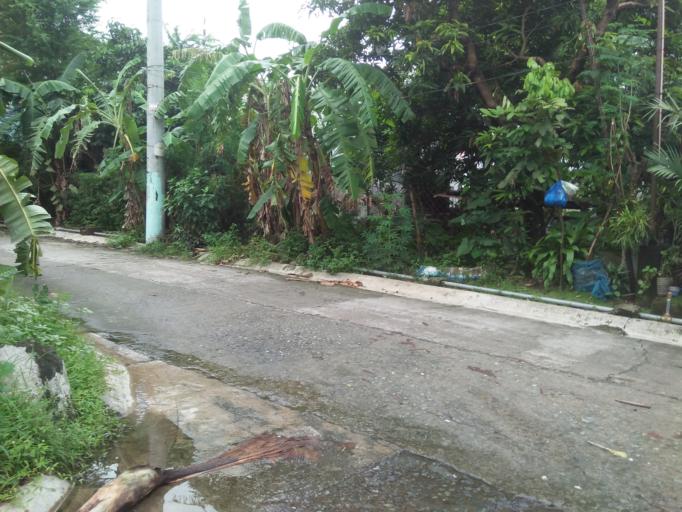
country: PH
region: Central Luzon
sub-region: Province of Bulacan
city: San Jose del Monte
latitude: 14.7481
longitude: 121.0651
